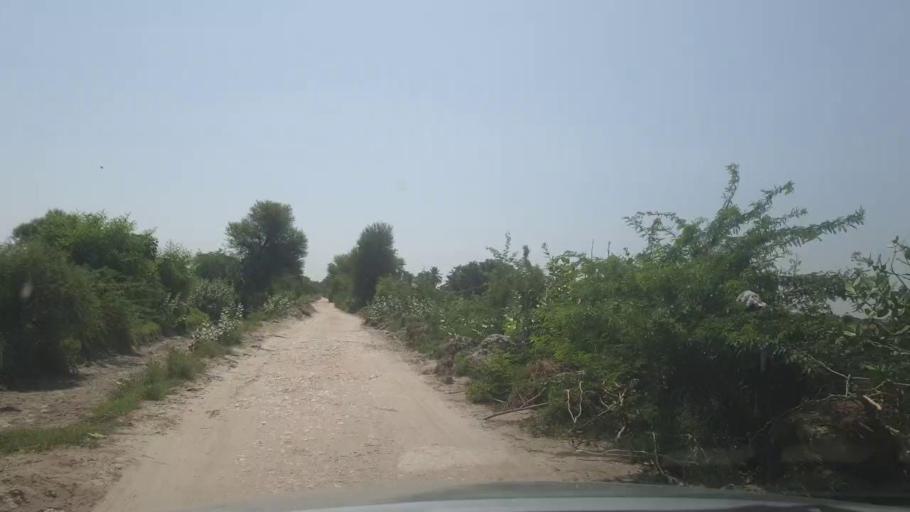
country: PK
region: Sindh
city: Khairpur
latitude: 27.3645
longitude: 69.0251
